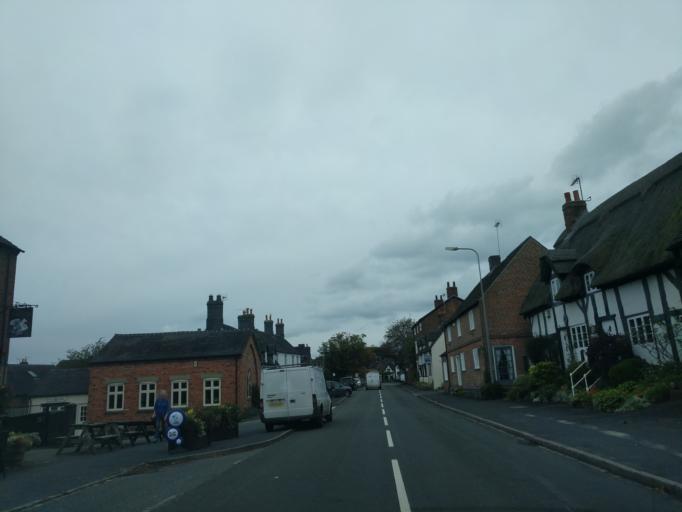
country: GB
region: England
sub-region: Cheshire East
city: Chorlton
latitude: 53.0340
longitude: -2.3683
